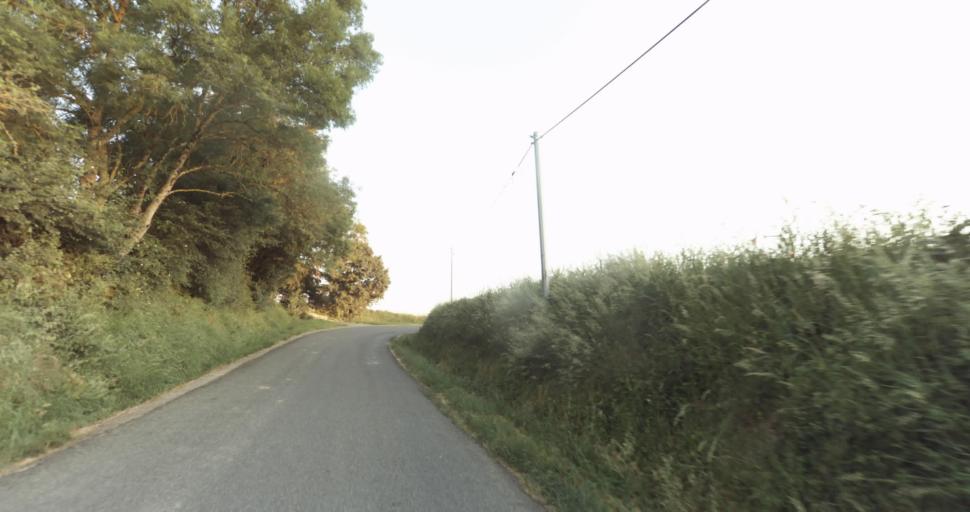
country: FR
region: Midi-Pyrenees
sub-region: Departement du Gers
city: Pujaudran
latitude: 43.6465
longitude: 1.1077
